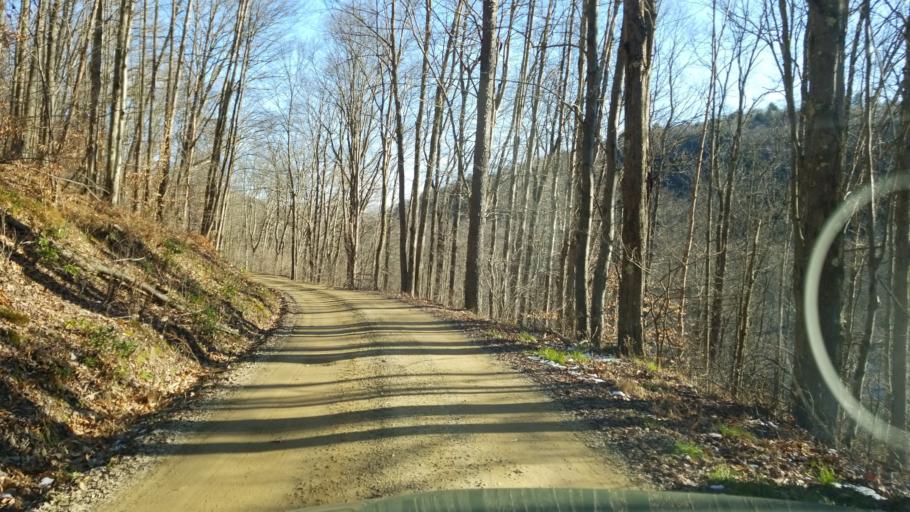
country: US
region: Pennsylvania
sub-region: Jefferson County
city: Brockway
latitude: 41.2898
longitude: -78.8344
